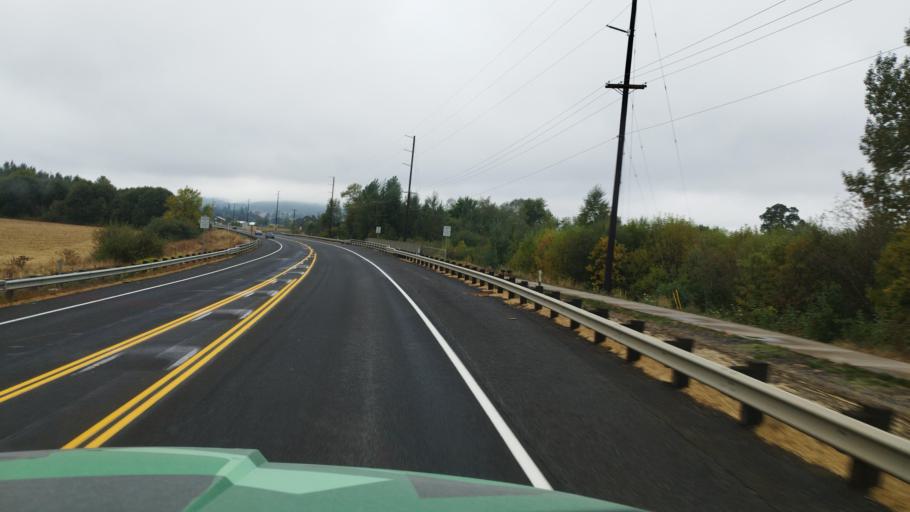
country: US
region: Oregon
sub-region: Washington County
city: Forest Grove
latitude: 45.5084
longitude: -123.1069
